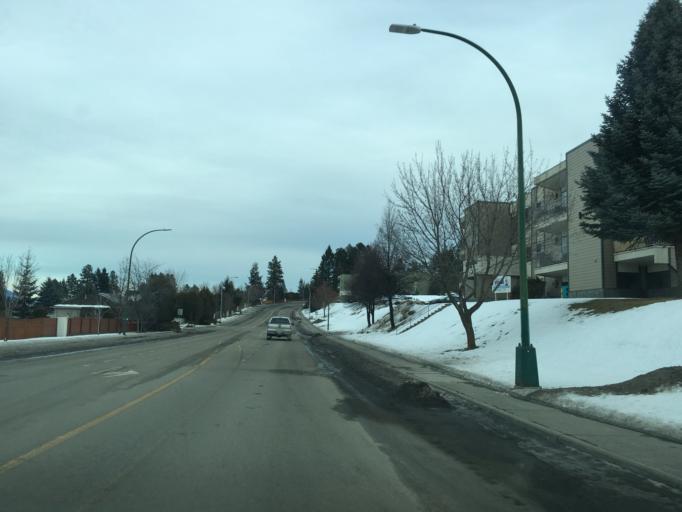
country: CA
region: British Columbia
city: Kamloops
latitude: 50.6487
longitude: -120.3656
